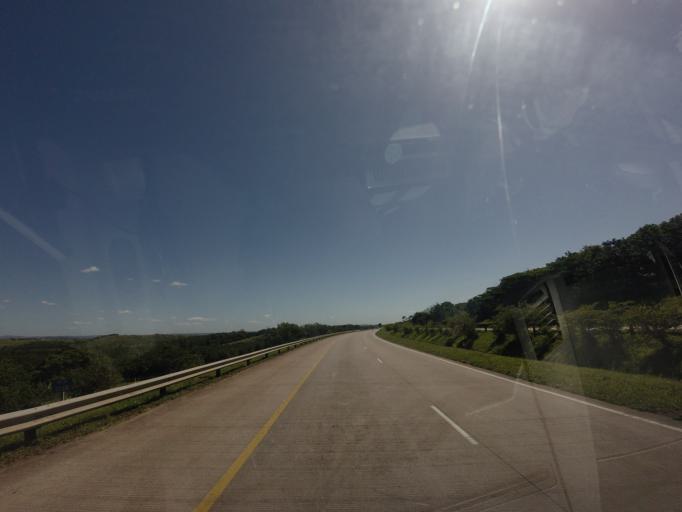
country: ZA
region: KwaZulu-Natal
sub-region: iLembe District Municipality
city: Ballitoville
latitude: -29.4724
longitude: 31.2332
